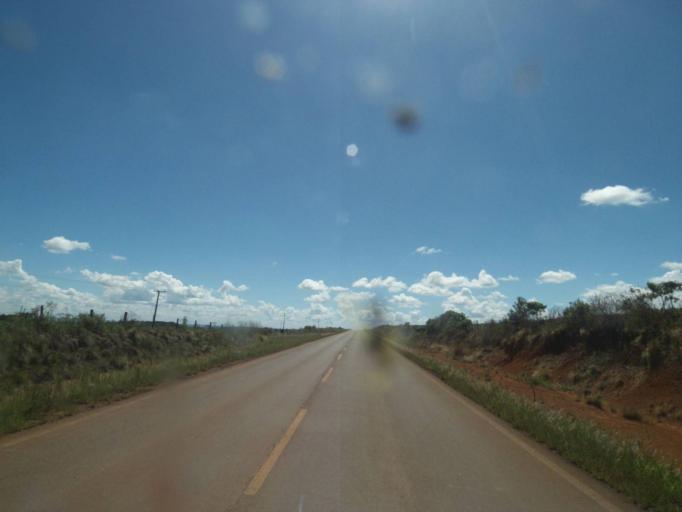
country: BR
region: Parana
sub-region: Pinhao
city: Pinhao
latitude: -25.8131
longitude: -52.0574
